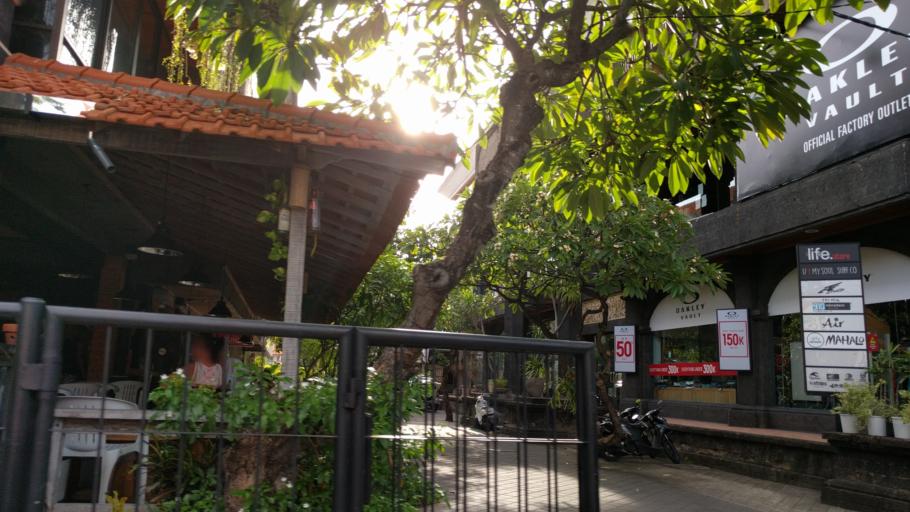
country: ID
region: Bali
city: Kuta
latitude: -8.7099
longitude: 115.1723
